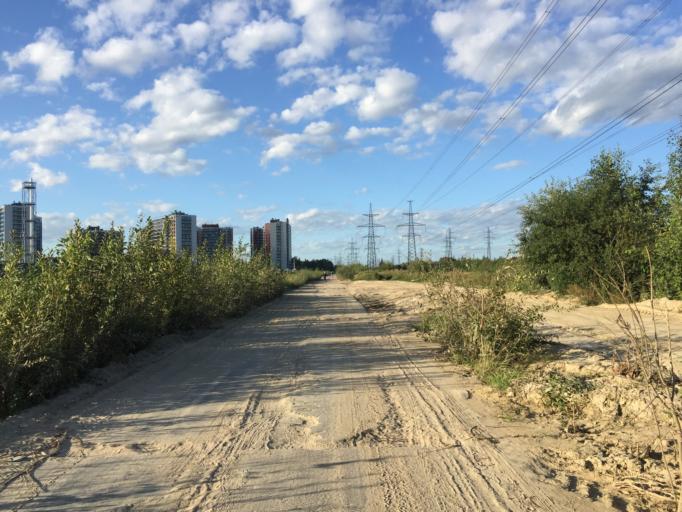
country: RU
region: Leningrad
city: Murino
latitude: 60.0646
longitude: 30.4480
